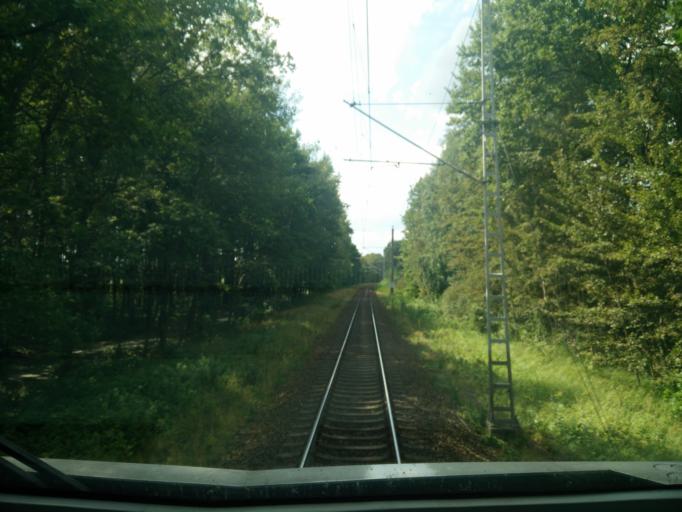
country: DE
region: Brandenburg
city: Kolkwitz
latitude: 51.7648
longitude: 14.2103
